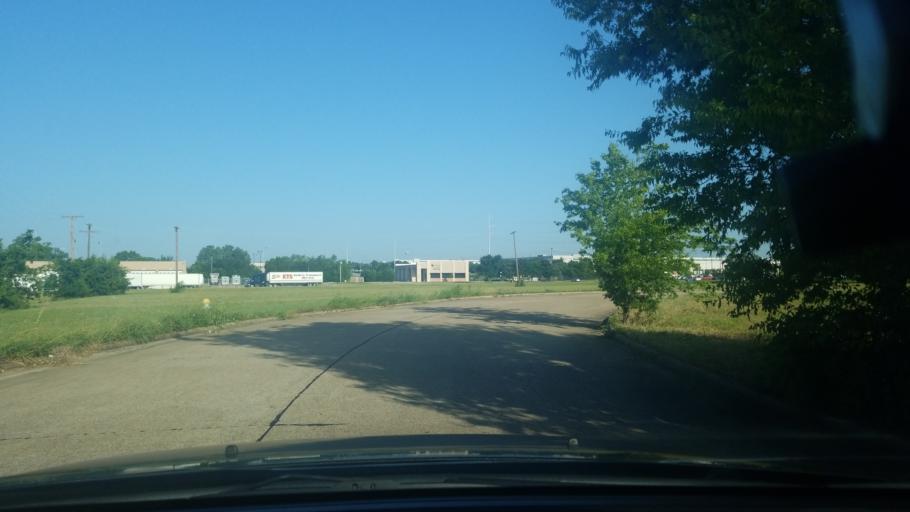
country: US
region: Texas
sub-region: Dallas County
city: Mesquite
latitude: 32.7911
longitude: -96.6726
